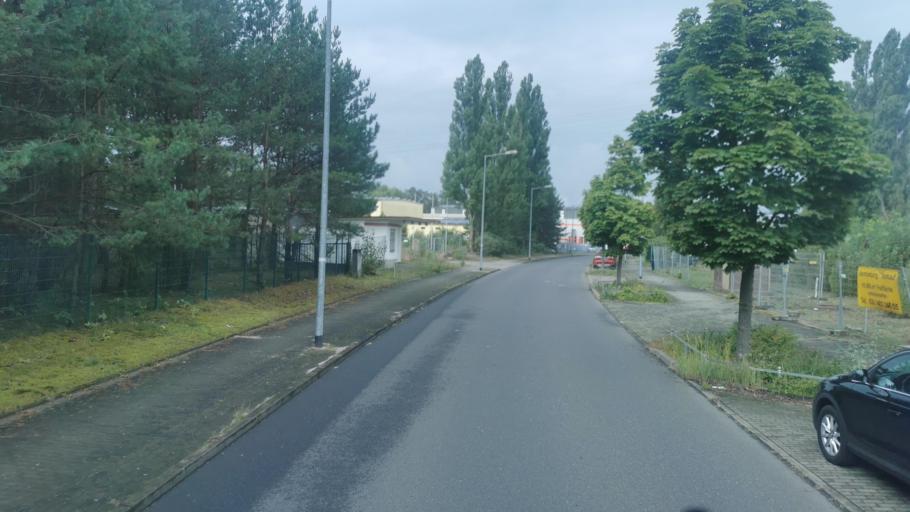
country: DE
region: Brandenburg
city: Eisenhuettenstadt
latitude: 52.1578
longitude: 14.6238
